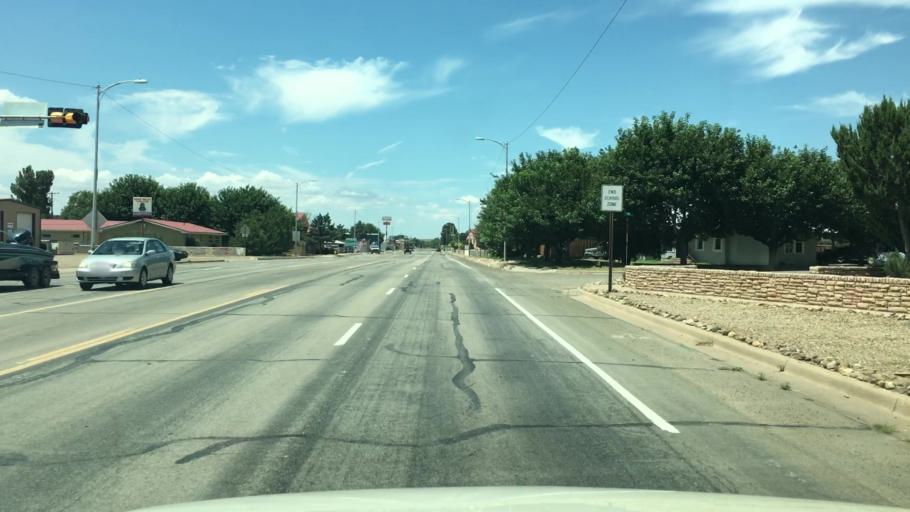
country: US
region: New Mexico
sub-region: De Baca County
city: Fort Sumner
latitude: 34.4697
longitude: -104.2388
